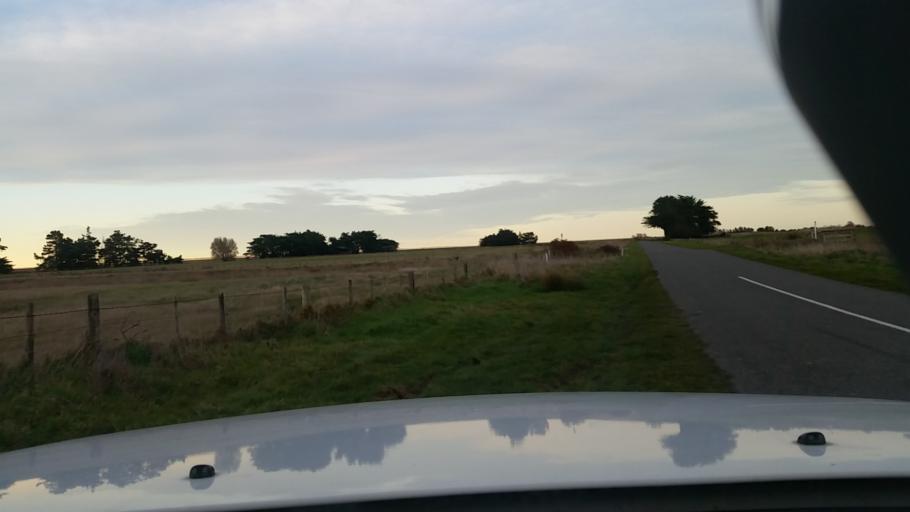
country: NZ
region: Canterbury
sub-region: Selwyn District
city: Lincoln
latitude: -43.7503
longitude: 172.6144
